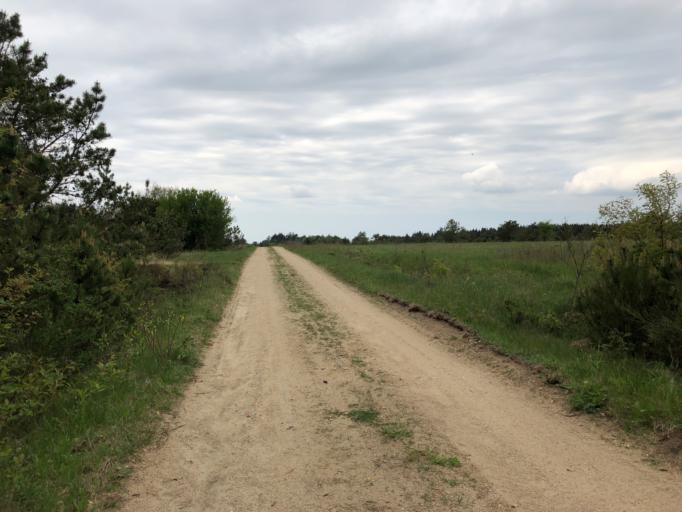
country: DK
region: Central Jutland
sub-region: Holstebro Kommune
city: Ulfborg
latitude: 56.2978
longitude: 8.4176
